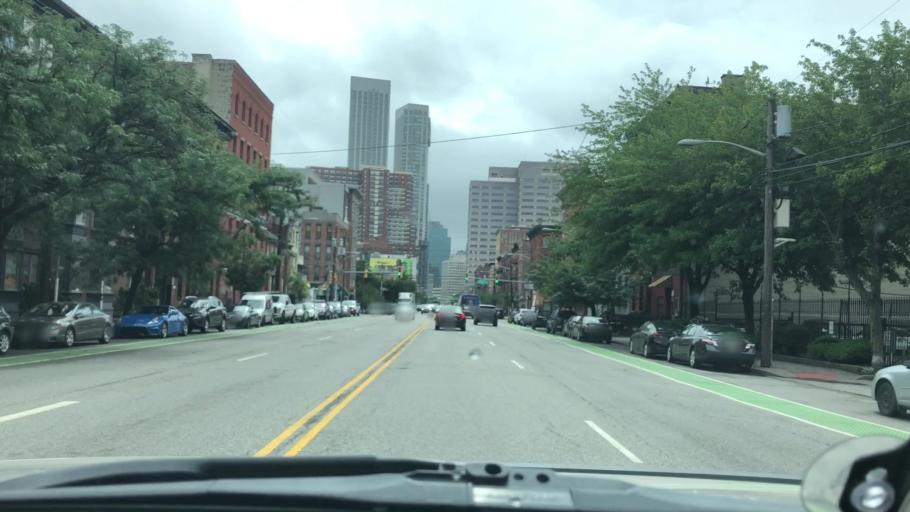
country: US
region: New Jersey
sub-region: Hudson County
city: Hoboken
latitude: 40.7210
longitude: -74.0479
